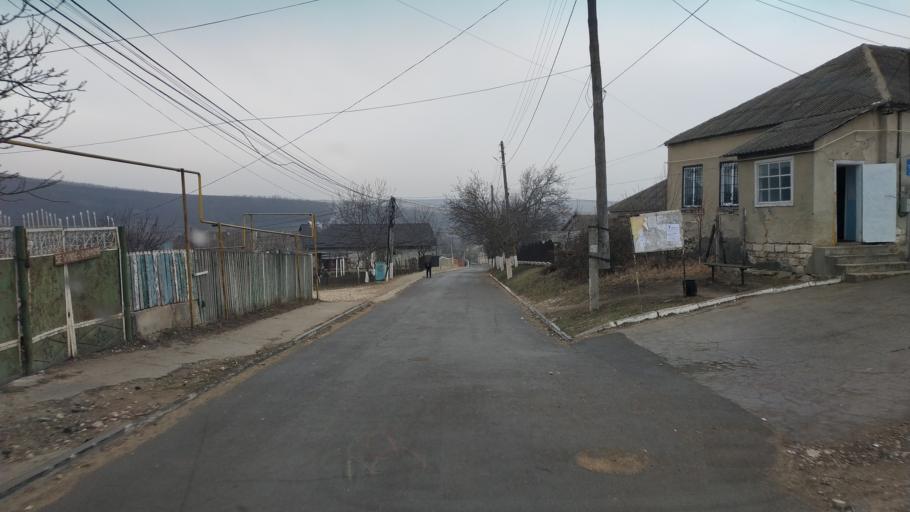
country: MD
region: Chisinau
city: Singera
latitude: 46.8306
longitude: 28.9730
